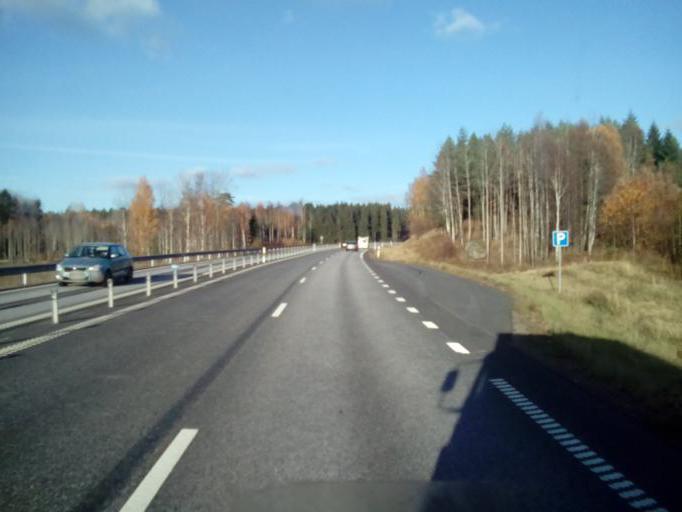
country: SE
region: Kalmar
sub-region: Vimmerby Kommun
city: Vimmerby
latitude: 57.7013
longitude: 16.0176
